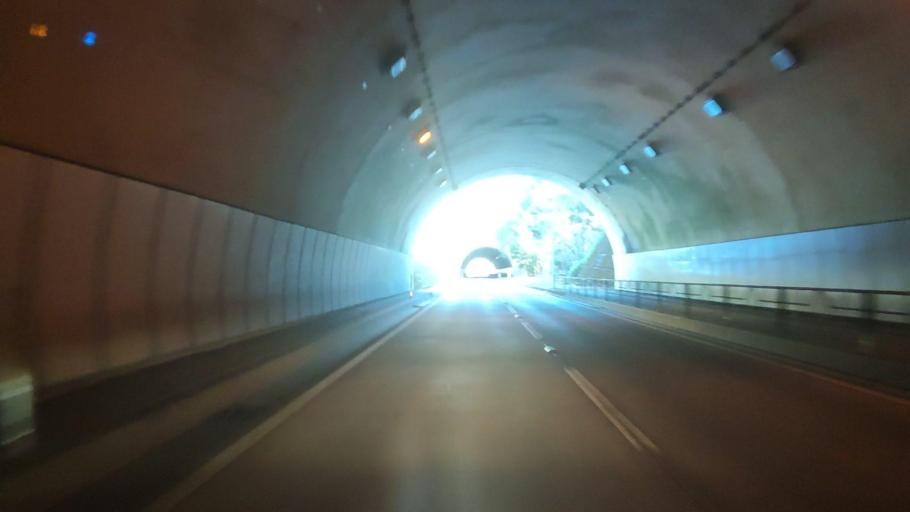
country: JP
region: Miyazaki
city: Nobeoka
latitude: 32.7004
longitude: 131.8149
